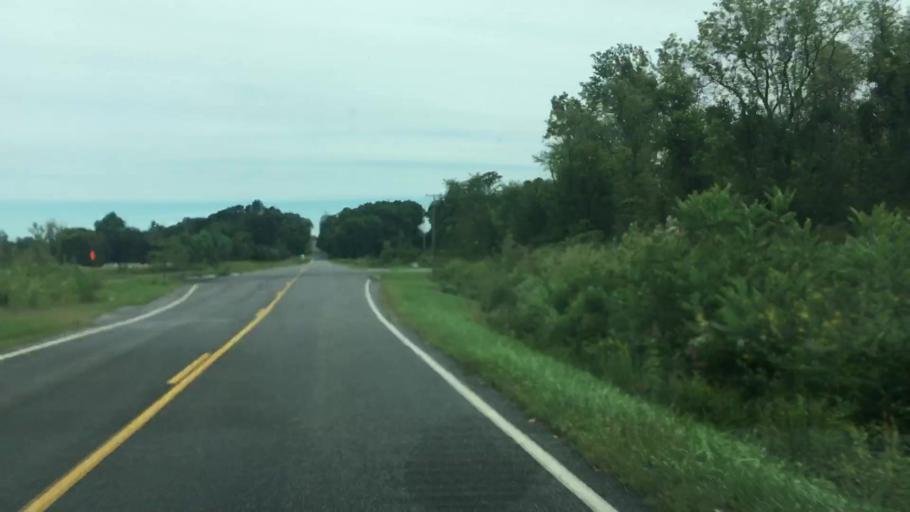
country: US
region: Michigan
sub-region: Kent County
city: Byron Center
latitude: 42.8259
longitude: -85.7828
